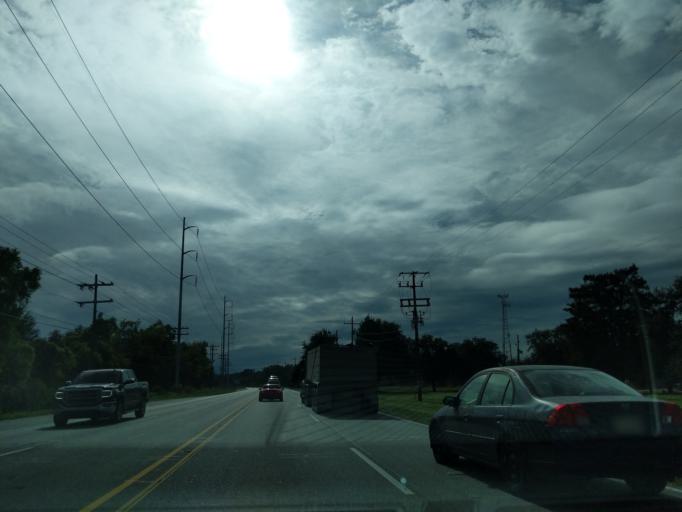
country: US
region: Louisiana
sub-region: Saint Bernard Parish
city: Chalmette
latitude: 30.0208
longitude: -89.9271
